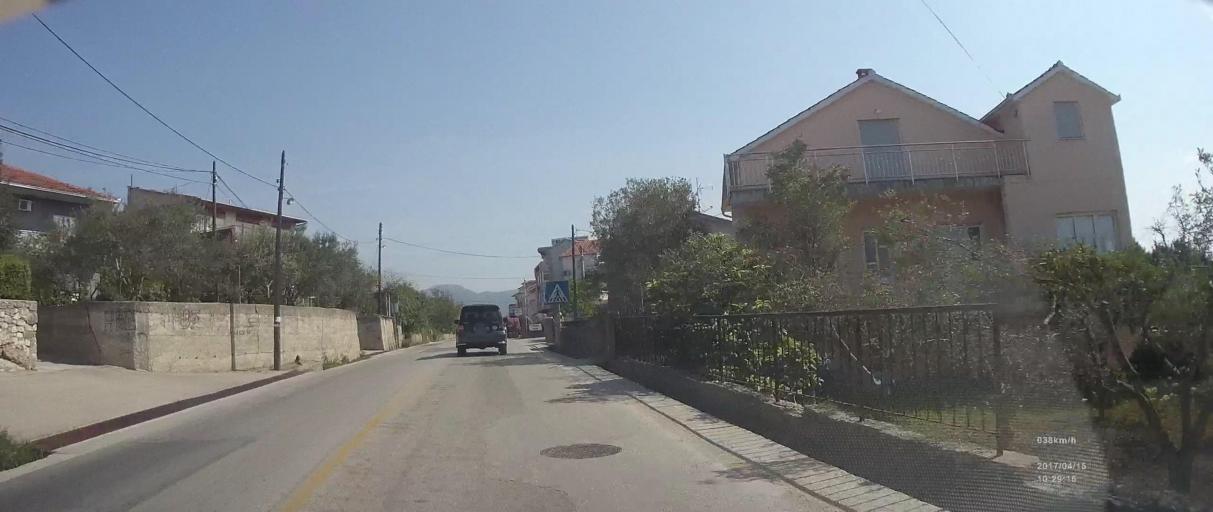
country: HR
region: Splitsko-Dalmatinska
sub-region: Grad Trogir
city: Trogir
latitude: 43.5232
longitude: 16.2652
